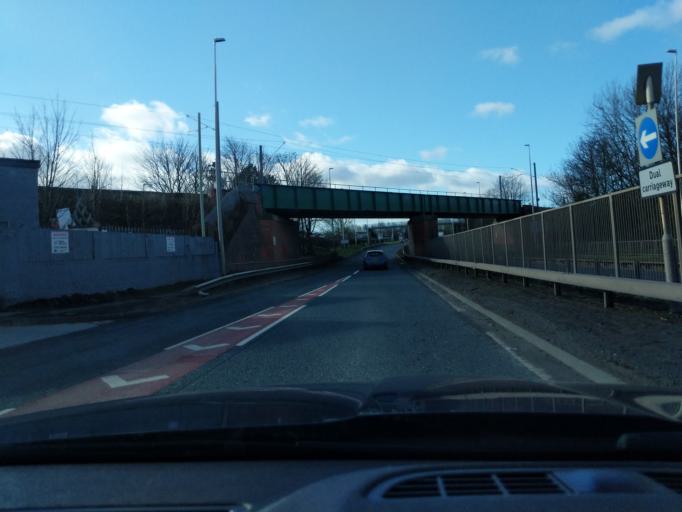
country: GB
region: England
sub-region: South Tyneside
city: Jarrow
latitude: 54.9572
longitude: -1.4938
